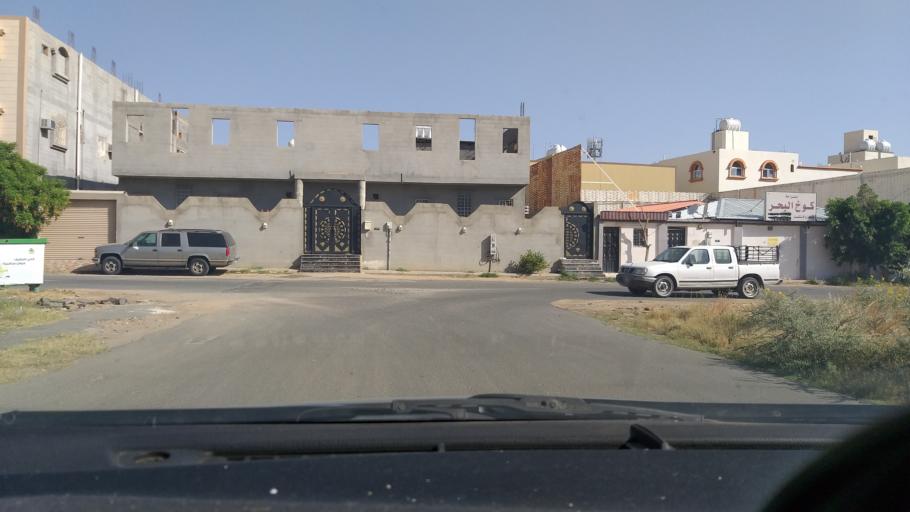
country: SA
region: Makkah
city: Ta'if
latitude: 21.2216
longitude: 40.3710
